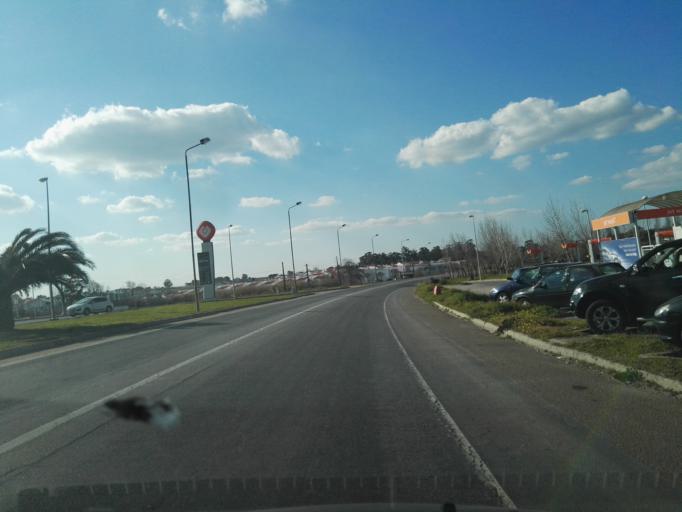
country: PT
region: Evora
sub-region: Evora
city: Evora
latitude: 38.5540
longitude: -7.9177
